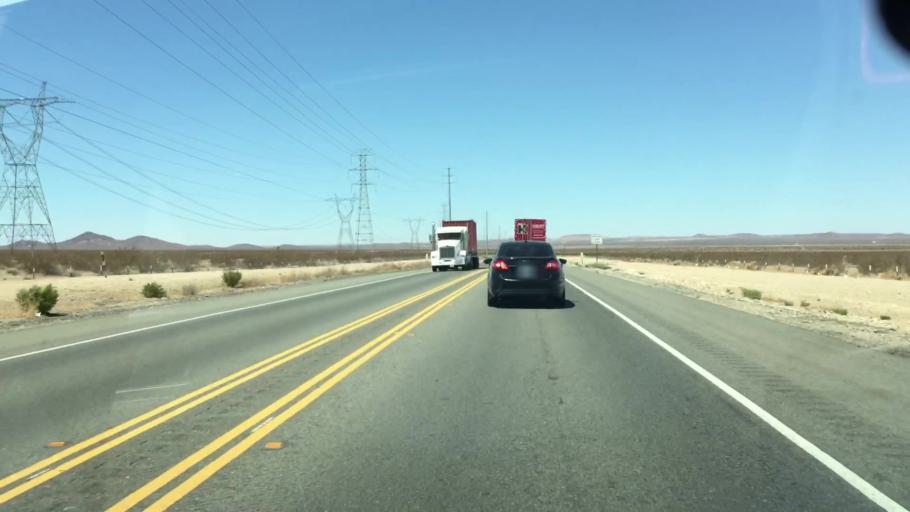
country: US
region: California
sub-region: San Bernardino County
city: Adelanto
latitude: 34.7559
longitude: -117.4723
